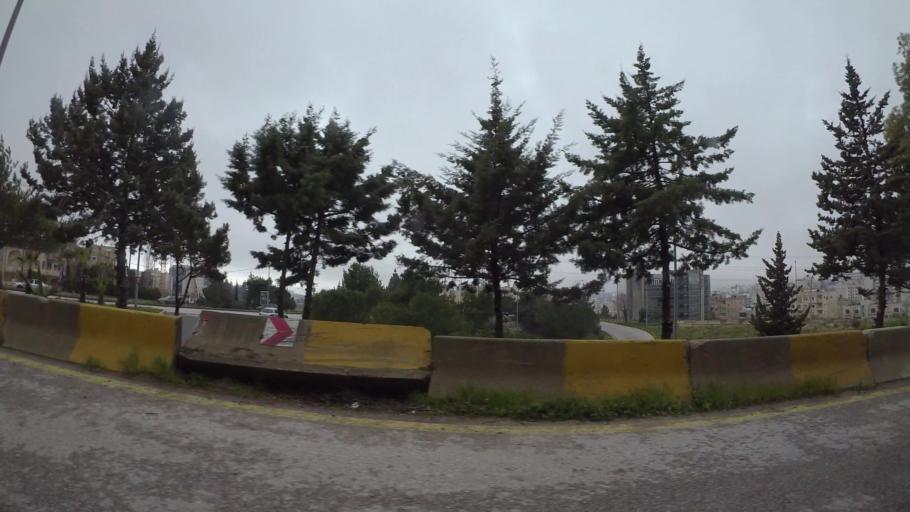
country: JO
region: Amman
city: Wadi as Sir
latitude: 31.9461
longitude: 35.8599
